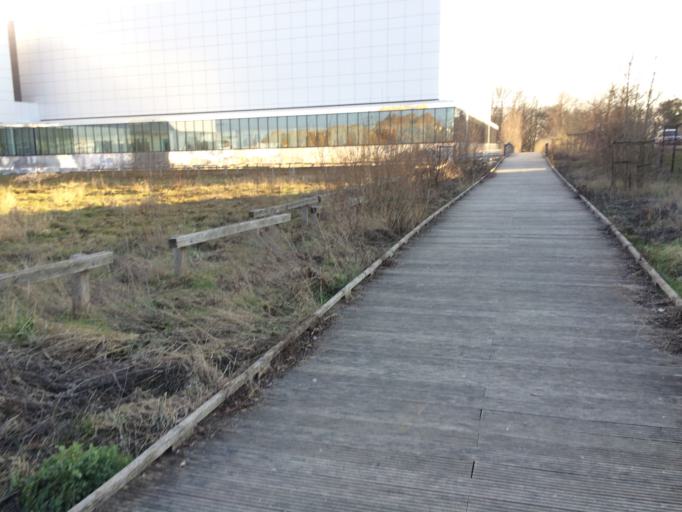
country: FR
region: Ile-de-France
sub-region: Departement de l'Essonne
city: Orsay
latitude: 48.7128
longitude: 2.1954
